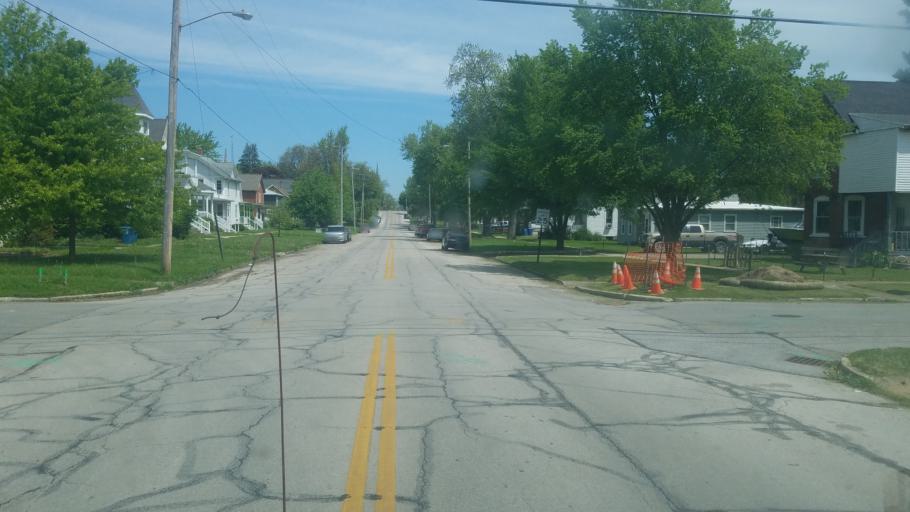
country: US
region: Ohio
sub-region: Sandusky County
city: Fremont
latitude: 41.3392
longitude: -83.1174
